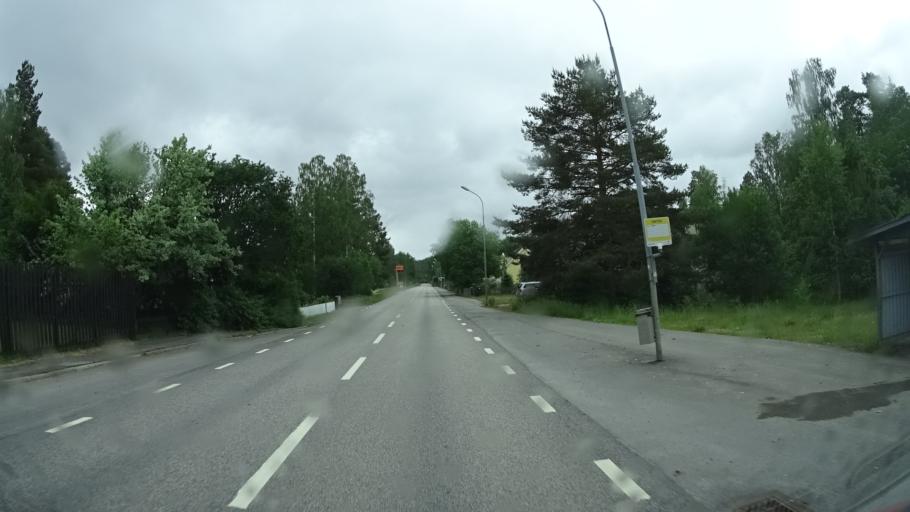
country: SE
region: Kalmar
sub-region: Hultsfreds Kommun
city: Hultsfred
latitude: 57.5409
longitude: 15.7561
